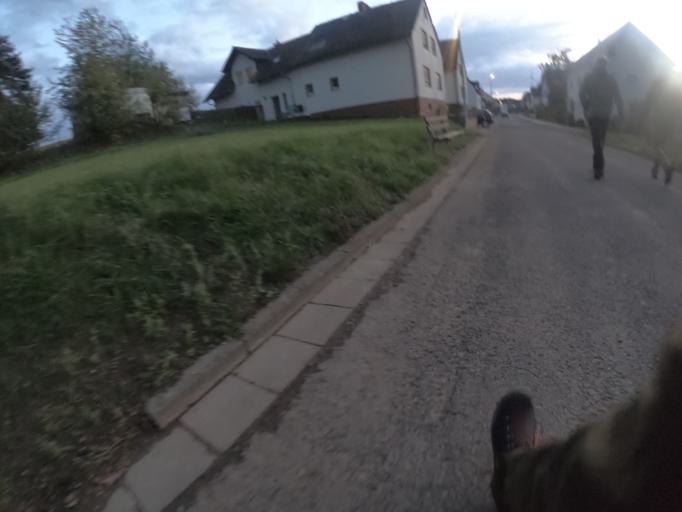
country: DE
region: Rheinland-Pfalz
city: Netzbach
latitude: 50.3301
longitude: 8.1565
